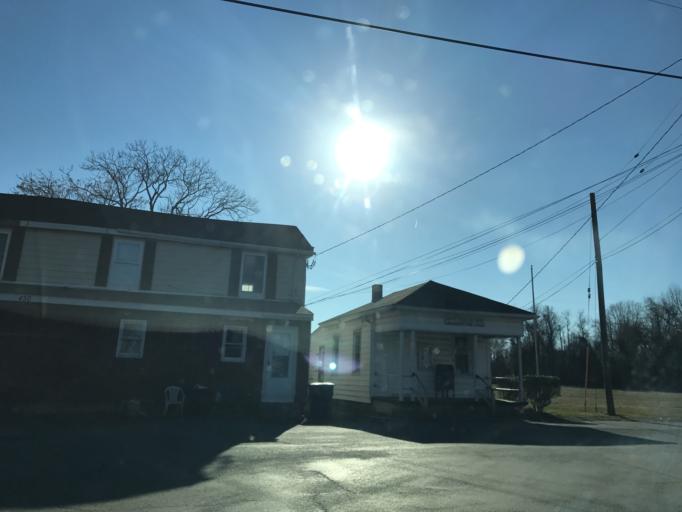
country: US
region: Maryland
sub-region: Harford County
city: Perryman
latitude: 39.4659
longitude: -76.2011
